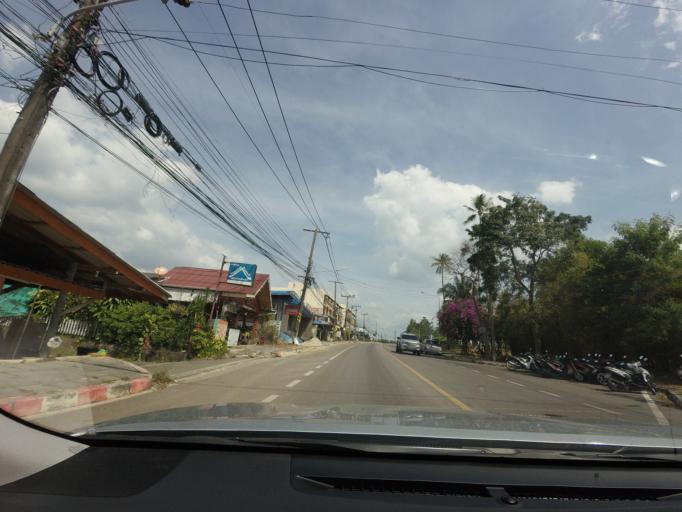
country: TH
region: Phangnga
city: Ban Ao Nang
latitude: 8.0556
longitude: 98.7510
